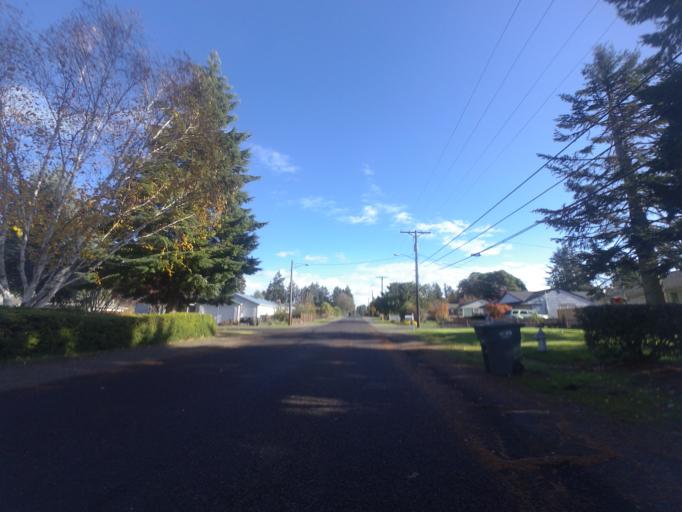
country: US
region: Washington
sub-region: Pierce County
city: University Place
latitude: 47.2280
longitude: -122.5554
